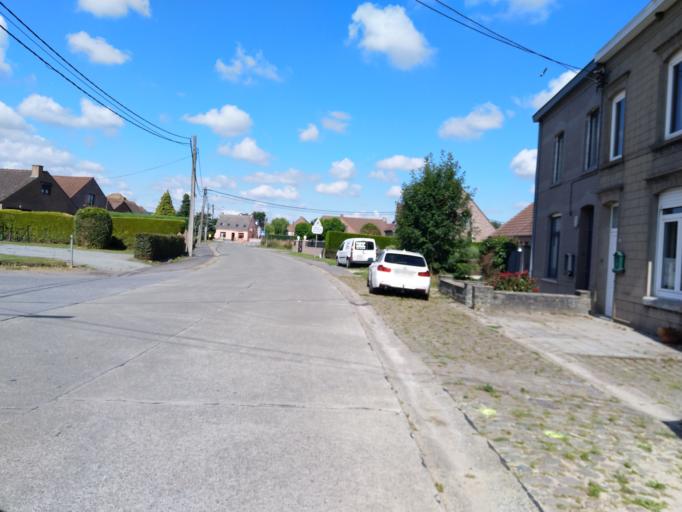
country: BE
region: Wallonia
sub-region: Province du Hainaut
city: Beloeil
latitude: 50.5917
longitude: 3.7457
